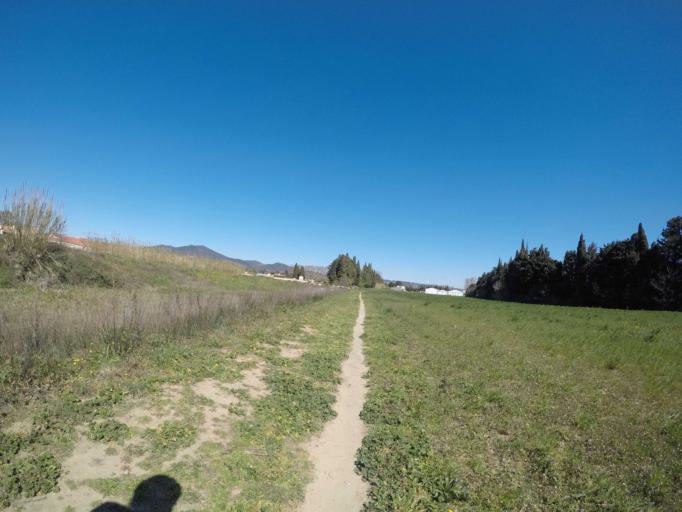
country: FR
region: Languedoc-Roussillon
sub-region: Departement des Pyrenees-Orientales
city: Corneilla-la-Riviere
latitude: 42.6814
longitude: 2.7259
